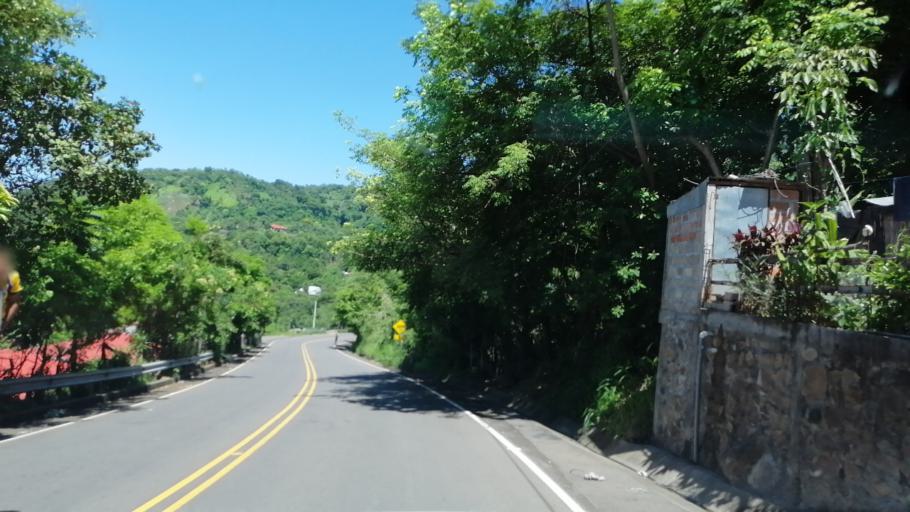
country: SV
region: San Miguel
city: Ciudad Barrios
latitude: 13.8148
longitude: -88.1853
